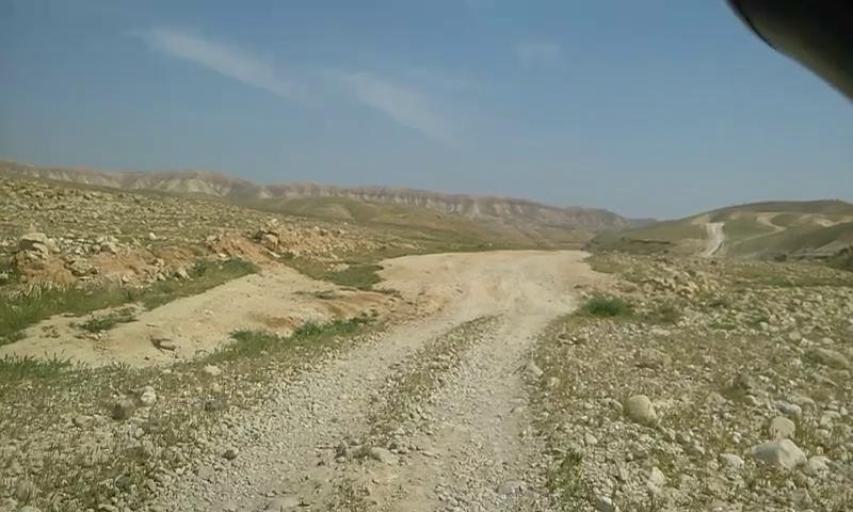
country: PS
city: `Arab ar Rashaydah
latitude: 31.5057
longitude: 35.2888
